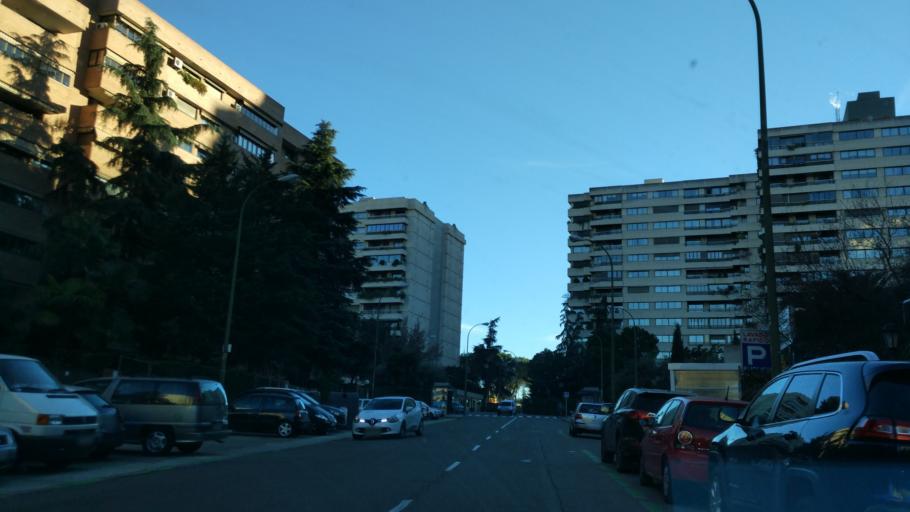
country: ES
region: Madrid
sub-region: Provincia de Madrid
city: Pinar de Chamartin
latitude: 40.4834
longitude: -3.6938
